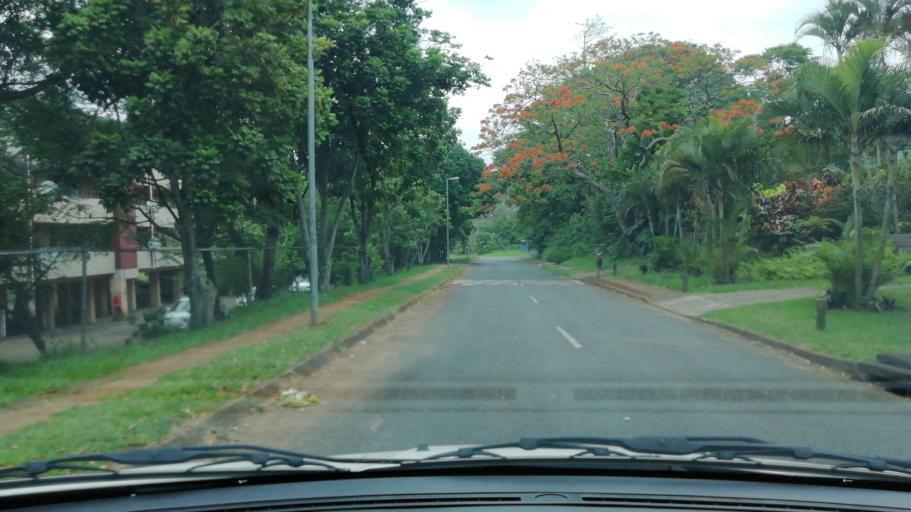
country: ZA
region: KwaZulu-Natal
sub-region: uThungulu District Municipality
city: Empangeni
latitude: -28.7536
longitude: 31.8916
